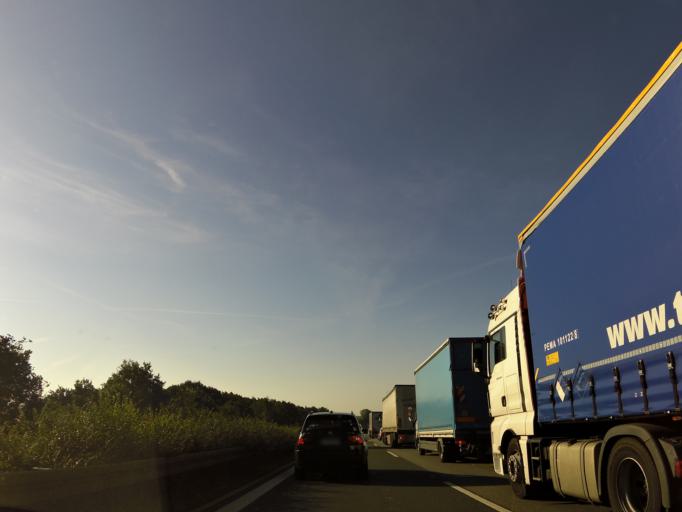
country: DE
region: Bavaria
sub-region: Regierungsbezirk Mittelfranken
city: Gremsdorf
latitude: 49.7104
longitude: 10.8463
